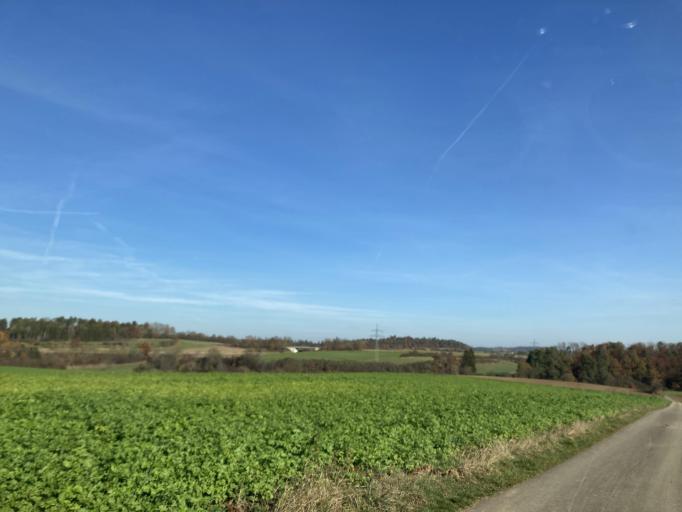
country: DE
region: Baden-Wuerttemberg
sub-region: Regierungsbezirk Stuttgart
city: Bondorf
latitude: 48.4937
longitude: 8.8822
